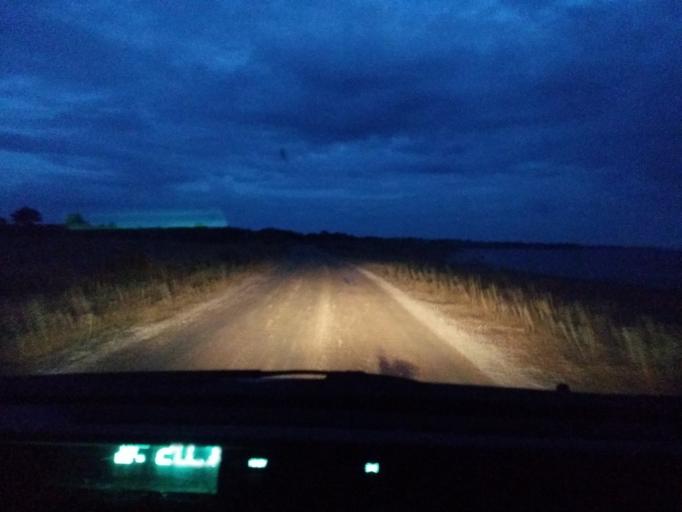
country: SE
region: Kalmar
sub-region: Borgholms Kommun
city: Borgholm
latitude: 57.1202
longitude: 16.8979
